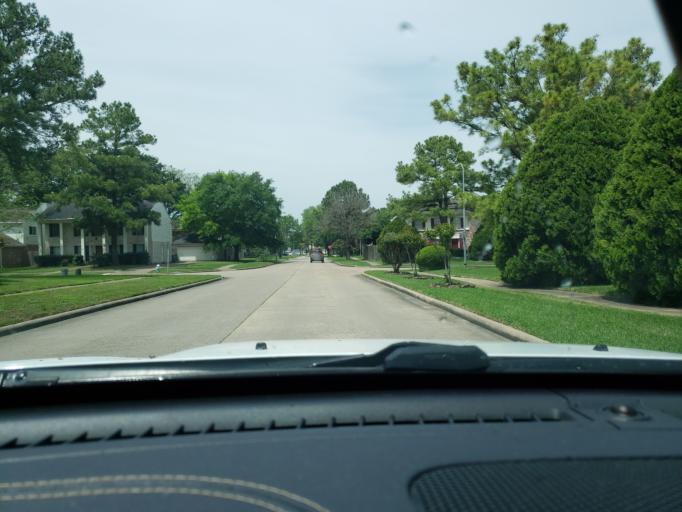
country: US
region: Texas
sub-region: Harris County
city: Jersey Village
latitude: 29.9180
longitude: -95.5747
